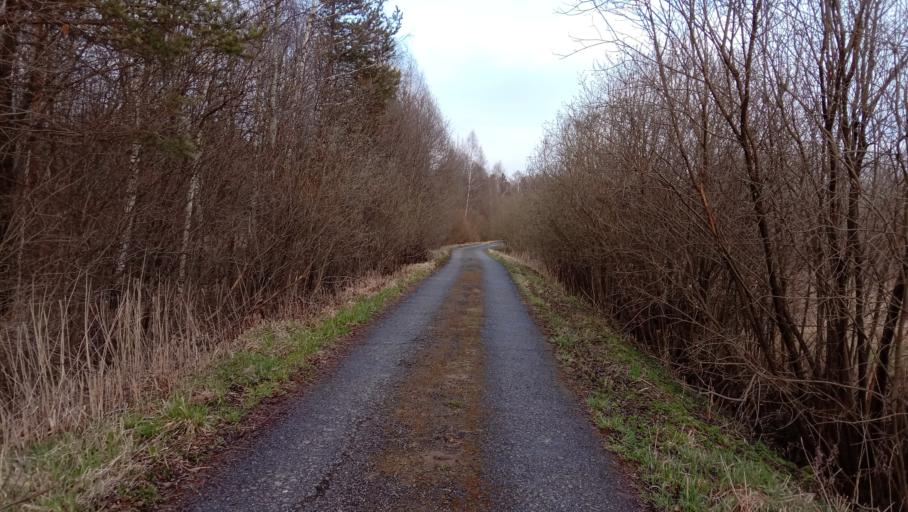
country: RU
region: Moskovskaya
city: Uvarovka
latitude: 55.7637
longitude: 35.7853
